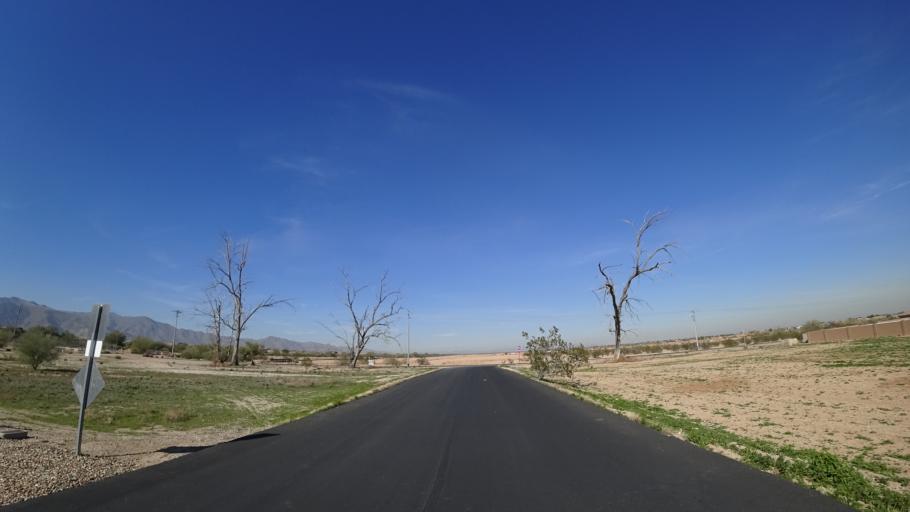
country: US
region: Arizona
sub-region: Maricopa County
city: Citrus Park
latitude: 33.5075
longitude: -112.4689
